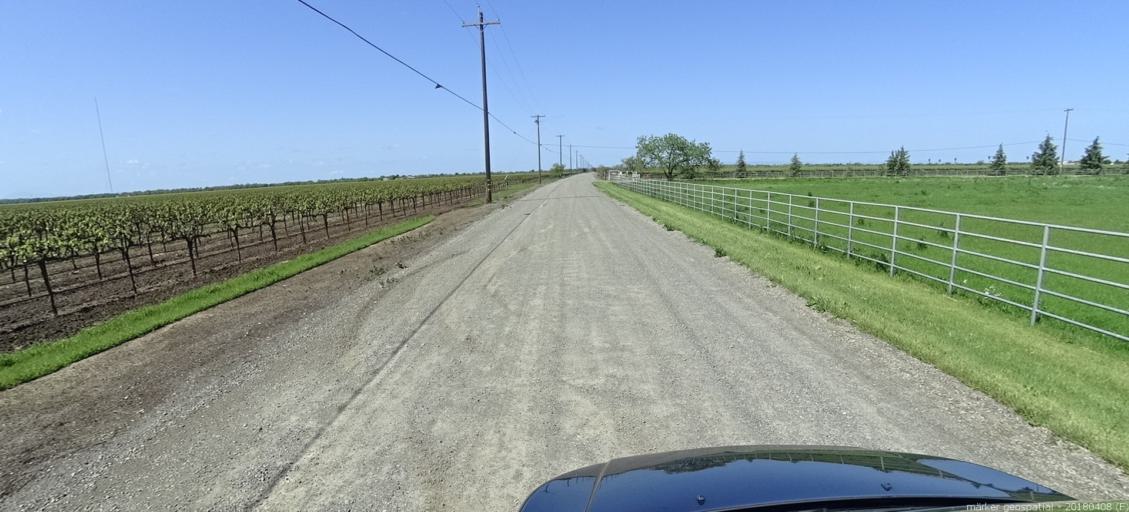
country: US
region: California
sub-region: Sacramento County
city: Walnut Grove
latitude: 38.2988
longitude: -121.4711
